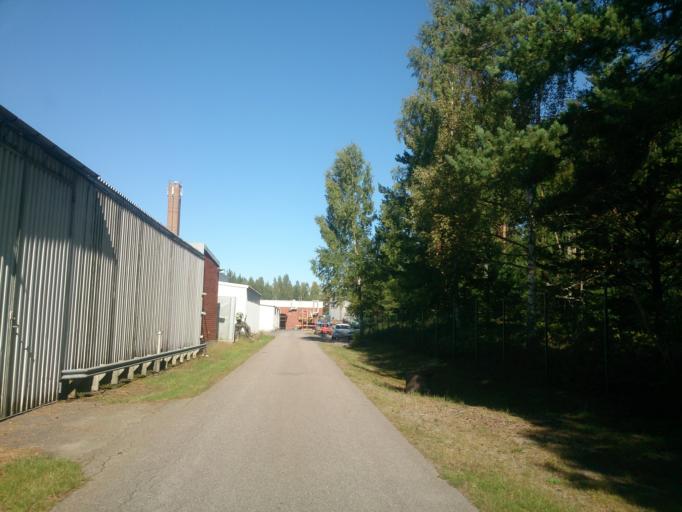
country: SE
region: OEstergoetland
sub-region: Atvidabergs Kommun
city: Atvidaberg
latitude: 58.2279
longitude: 15.9762
